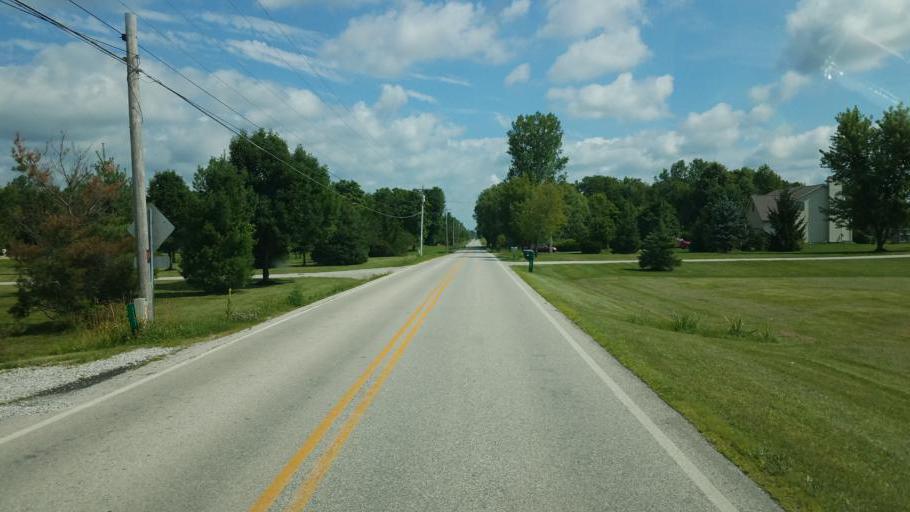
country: US
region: Ohio
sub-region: Delaware County
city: Sunbury
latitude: 40.2828
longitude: -82.9357
